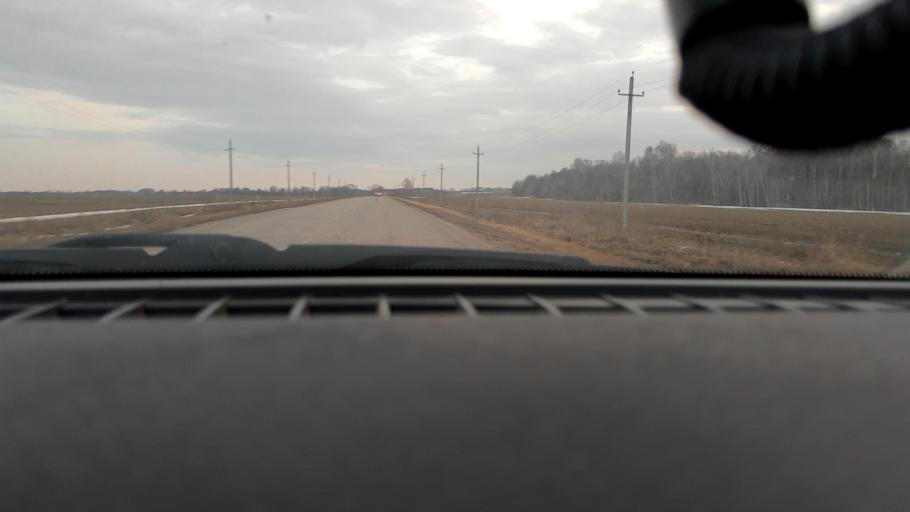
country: RU
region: Bashkortostan
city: Iglino
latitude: 54.6973
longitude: 56.4168
